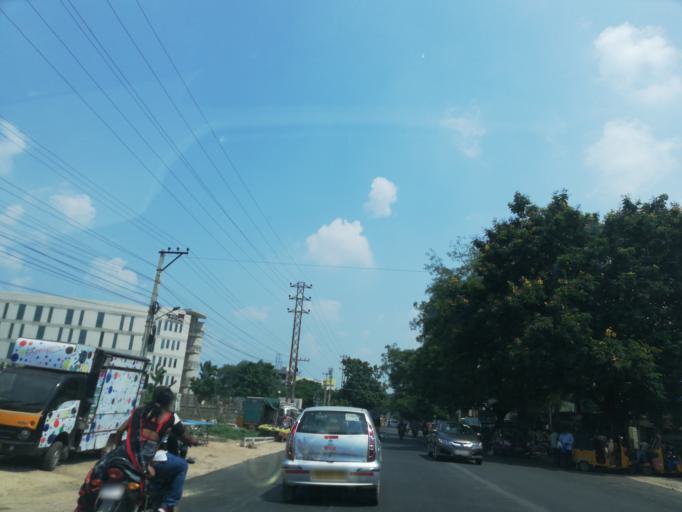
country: IN
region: Telangana
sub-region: Medak
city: Serilingampalle
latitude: 17.4809
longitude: 78.3201
